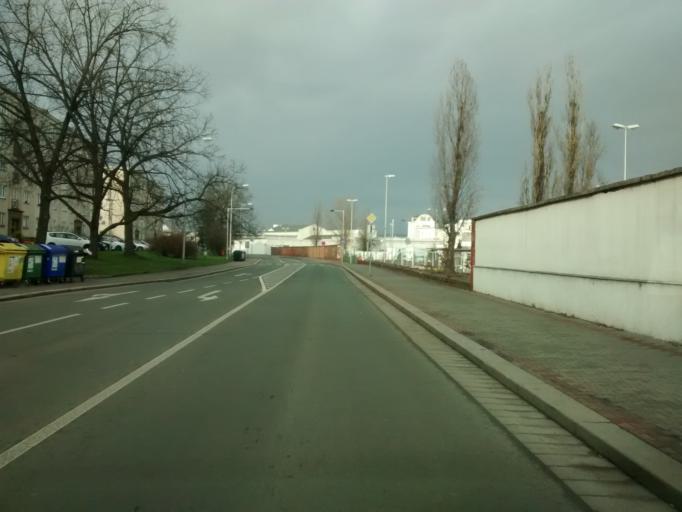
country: CZ
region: Central Bohemia
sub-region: Okres Mlada Boleslav
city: Mlada Boleslav
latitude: 50.4148
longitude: 14.9187
